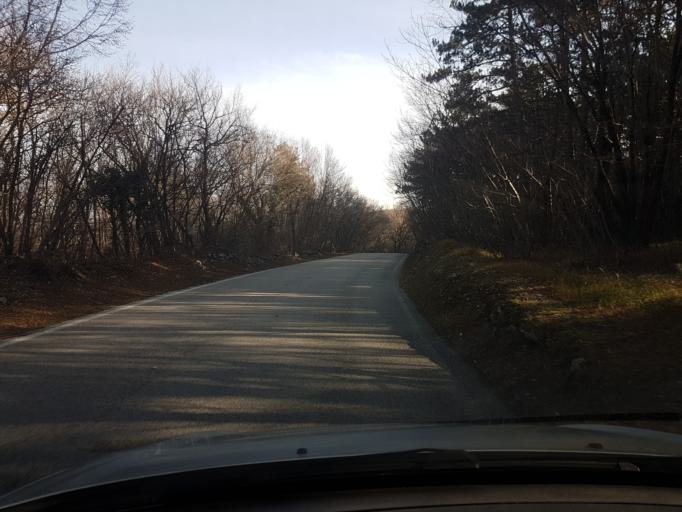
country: IT
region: Friuli Venezia Giulia
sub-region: Provincia di Trieste
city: Aurisina Cave
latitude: 45.7811
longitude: 13.6684
